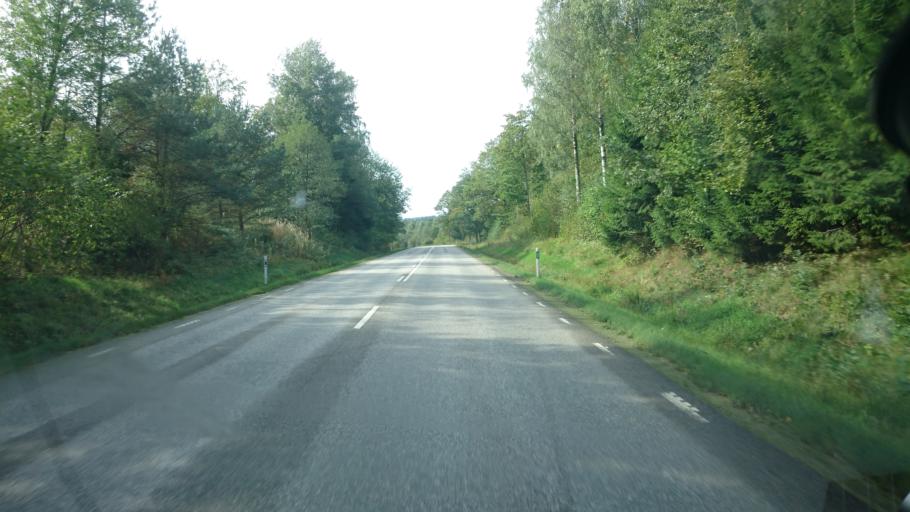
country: SE
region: Vaestra Goetaland
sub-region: Alingsas Kommun
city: Sollebrunn
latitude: 58.0627
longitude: 12.4713
